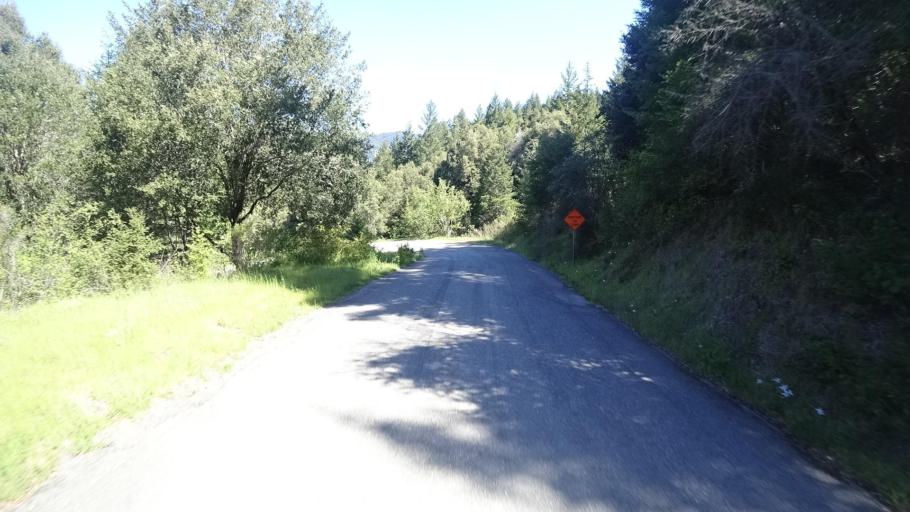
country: US
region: California
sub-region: Humboldt County
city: Rio Dell
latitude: 40.2194
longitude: -124.1112
